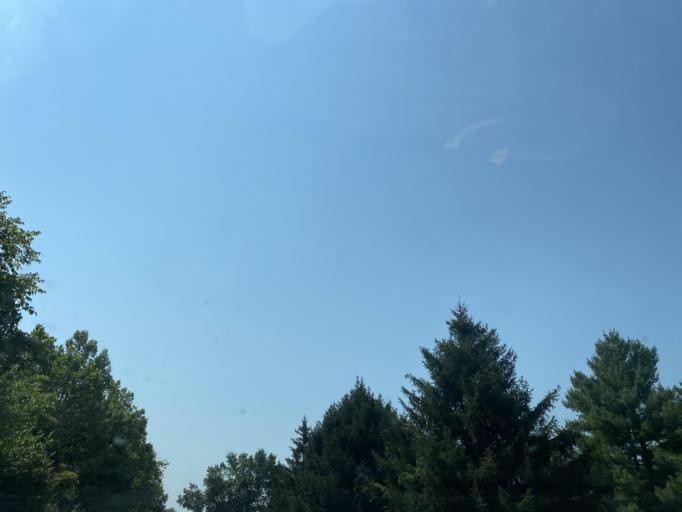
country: US
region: Kentucky
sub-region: Campbell County
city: Claryville
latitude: 38.8420
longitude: -84.4607
